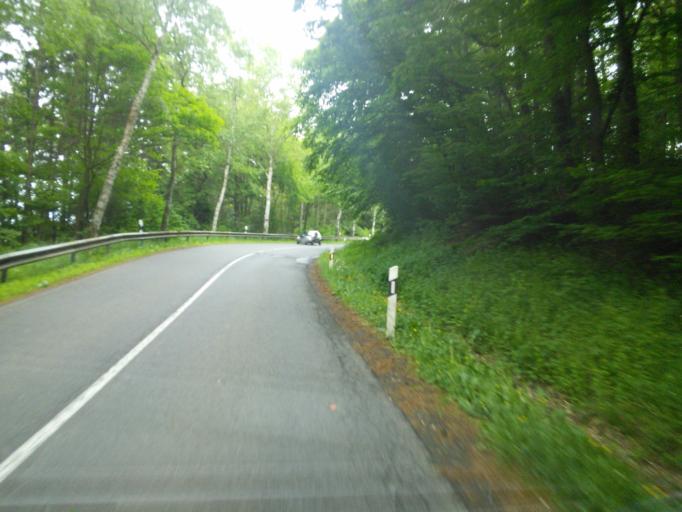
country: DE
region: Rheinland-Pfalz
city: Berg
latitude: 50.5778
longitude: 6.9149
